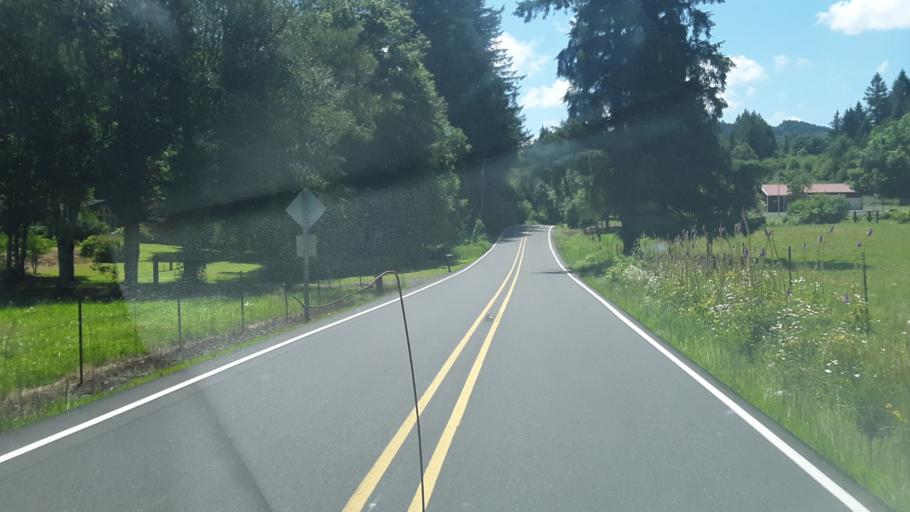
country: US
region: Washington
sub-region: Clark County
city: Amboy
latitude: 45.9387
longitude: -122.3798
